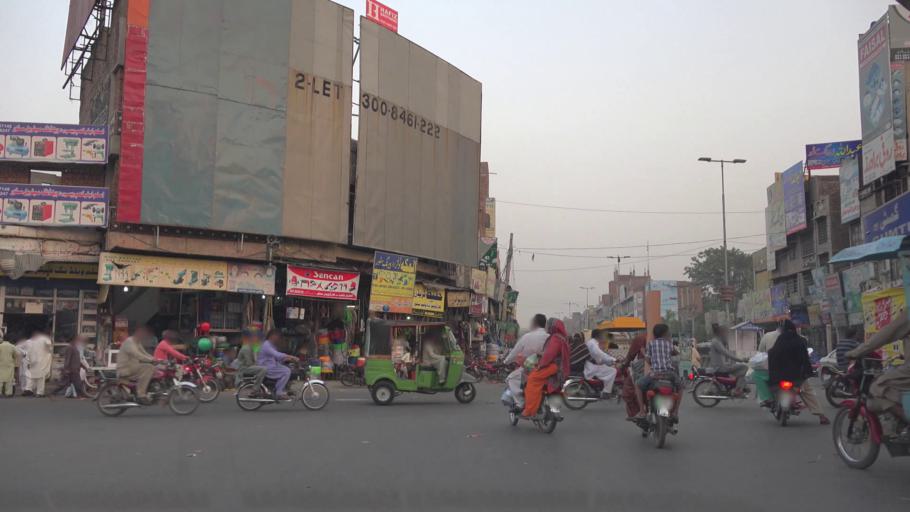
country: PK
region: Punjab
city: Faisalabad
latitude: 31.4201
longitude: 73.0832
